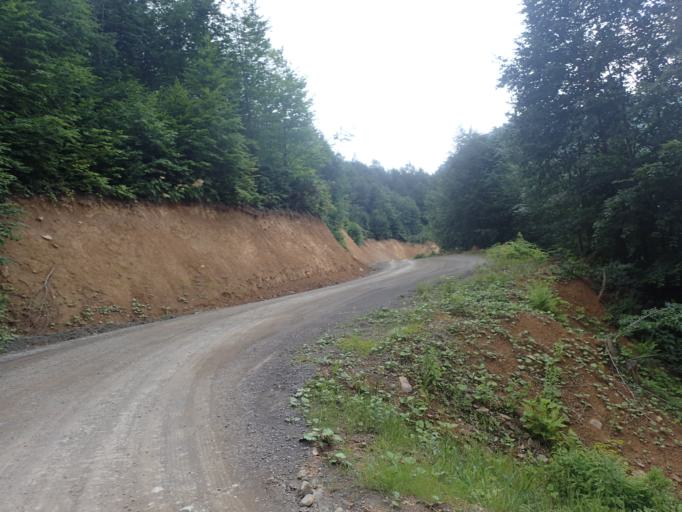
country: TR
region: Ordu
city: Akkus
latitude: 40.8575
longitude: 37.0061
